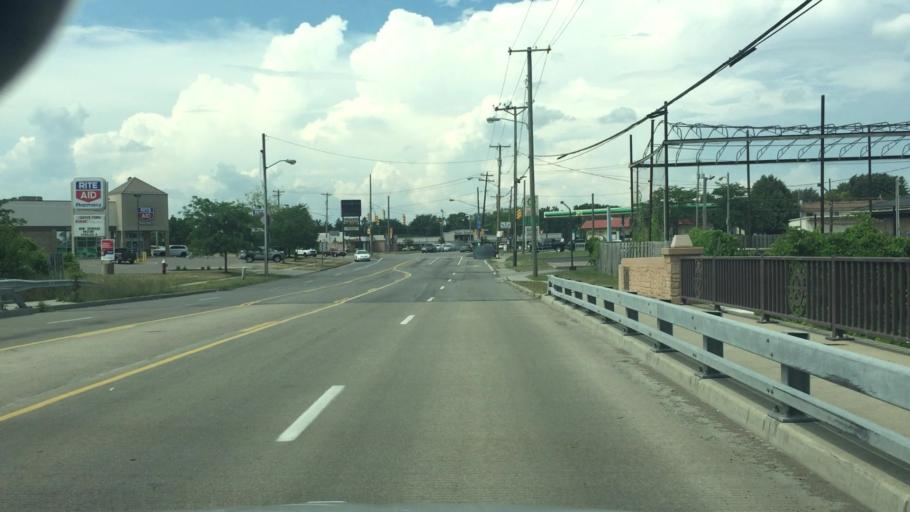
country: US
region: Ohio
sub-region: Lucas County
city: Oregon
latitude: 41.7105
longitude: -83.4997
